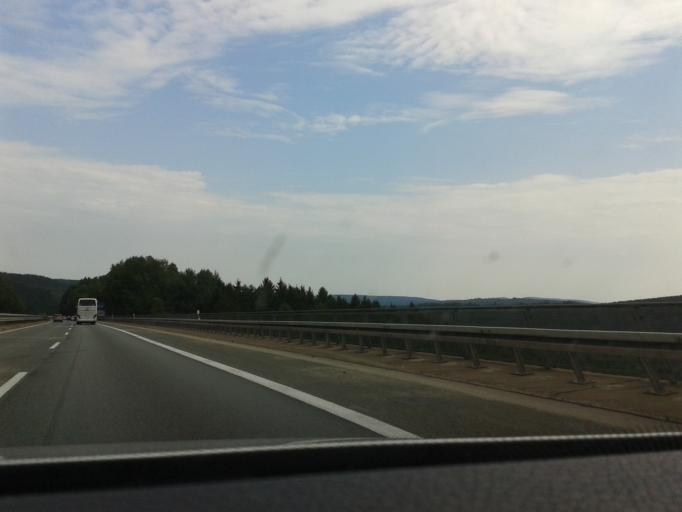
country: DE
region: North Rhine-Westphalia
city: Marsberg
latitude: 51.5236
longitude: 8.9169
